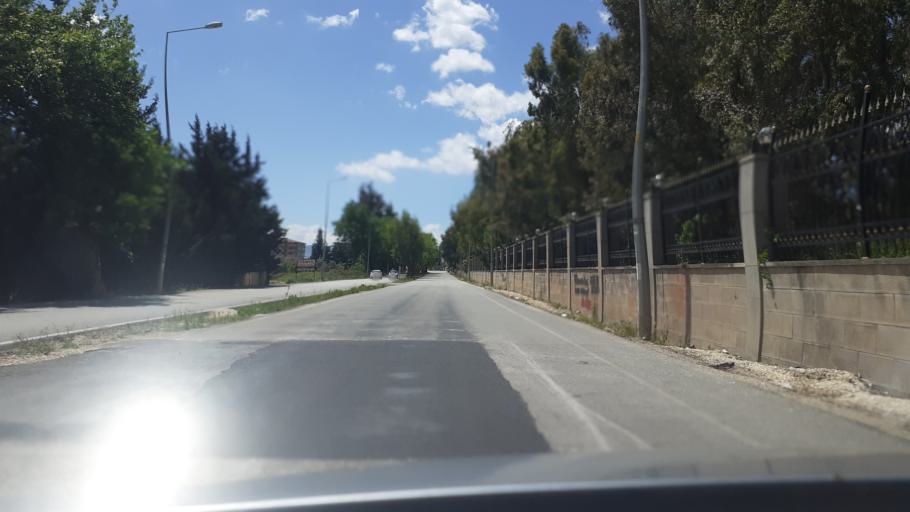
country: TR
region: Hatay
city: Anayazi
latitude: 36.3240
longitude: 36.1983
